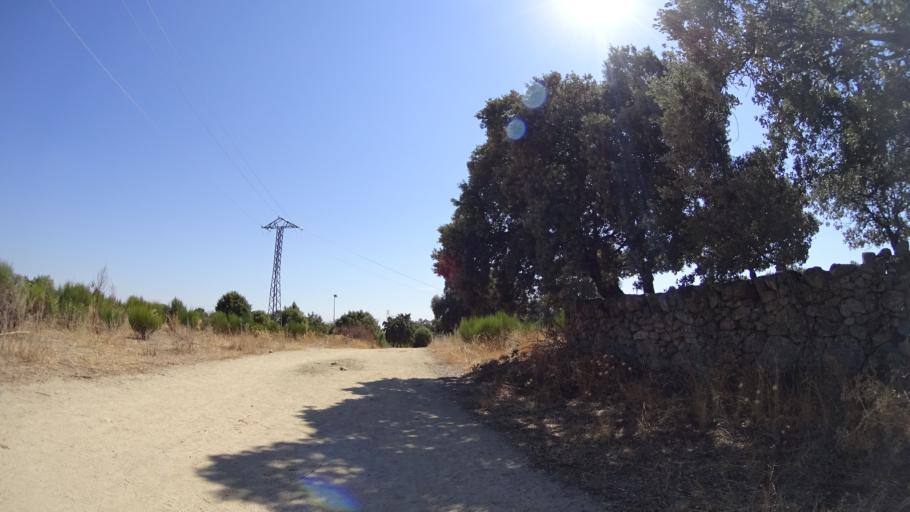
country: ES
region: Madrid
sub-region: Provincia de Madrid
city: Galapagar
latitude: 40.6034
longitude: -4.0103
